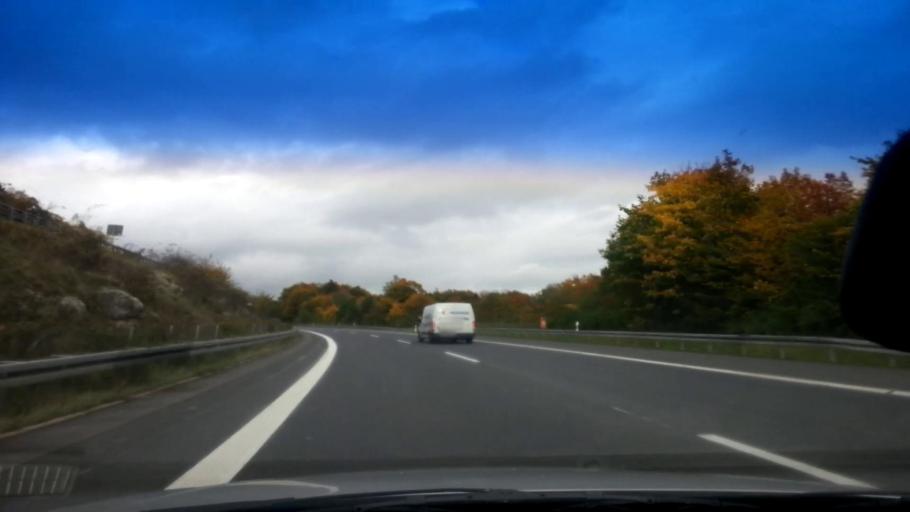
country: DE
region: Bavaria
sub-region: Upper Franconia
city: Poxdorf
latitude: 49.9841
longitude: 11.0950
